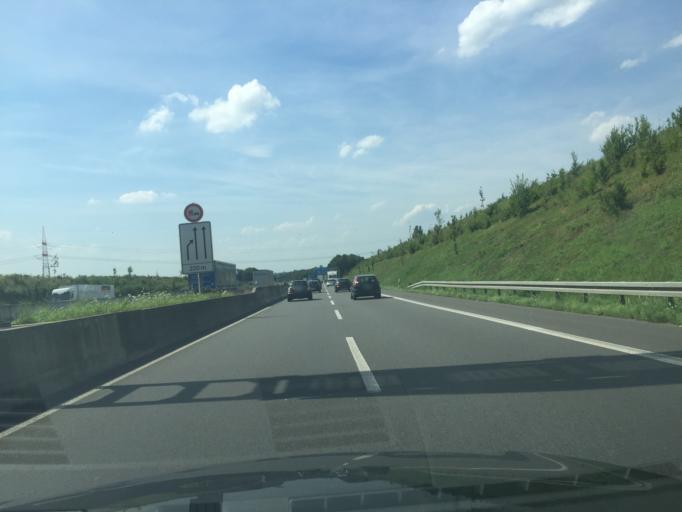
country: DE
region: North Rhine-Westphalia
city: Witten
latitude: 51.4968
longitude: 7.3952
